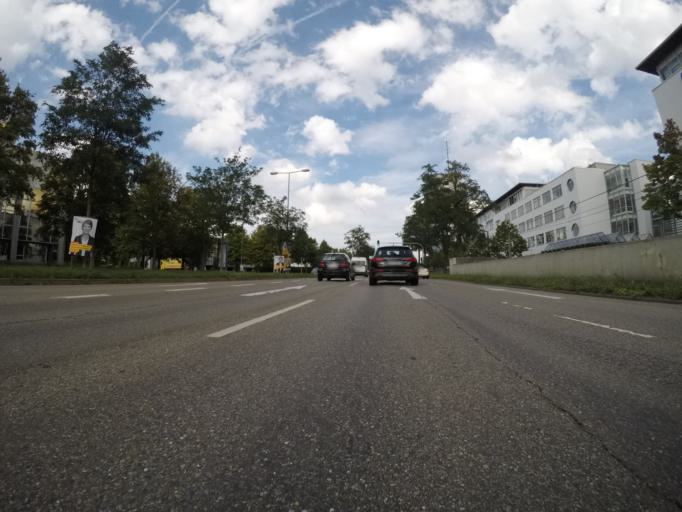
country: DE
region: Baden-Wuerttemberg
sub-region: Regierungsbezirk Stuttgart
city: Stuttgart
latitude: 48.7467
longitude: 9.1636
